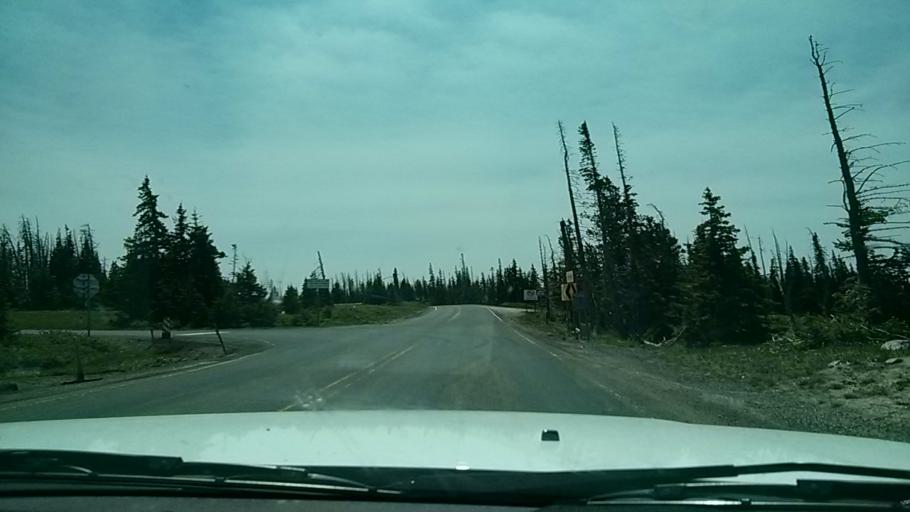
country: US
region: Utah
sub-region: Iron County
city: Parowan
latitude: 37.6547
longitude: -112.8265
